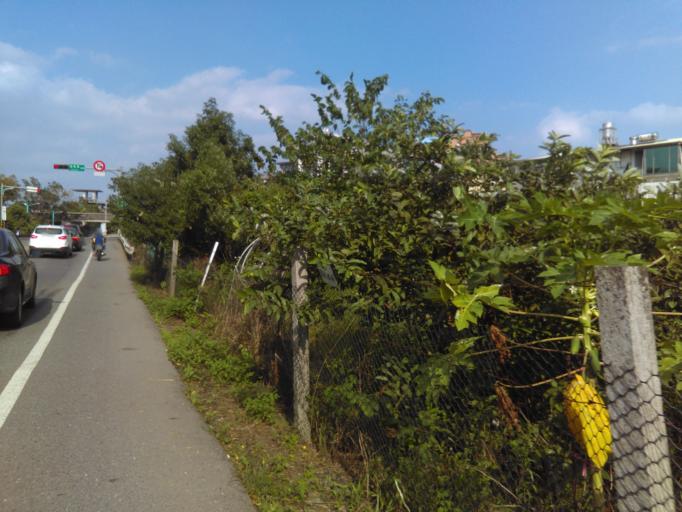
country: TW
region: Taiwan
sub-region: Yilan
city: Yilan
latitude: 24.7608
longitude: 121.7485
